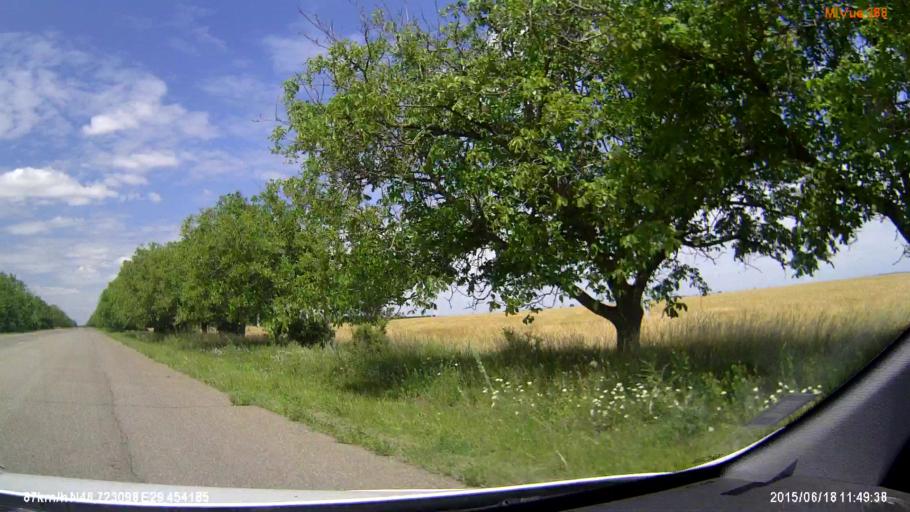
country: MD
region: Causeni
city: Causeni
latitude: 46.7227
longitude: 29.4542
